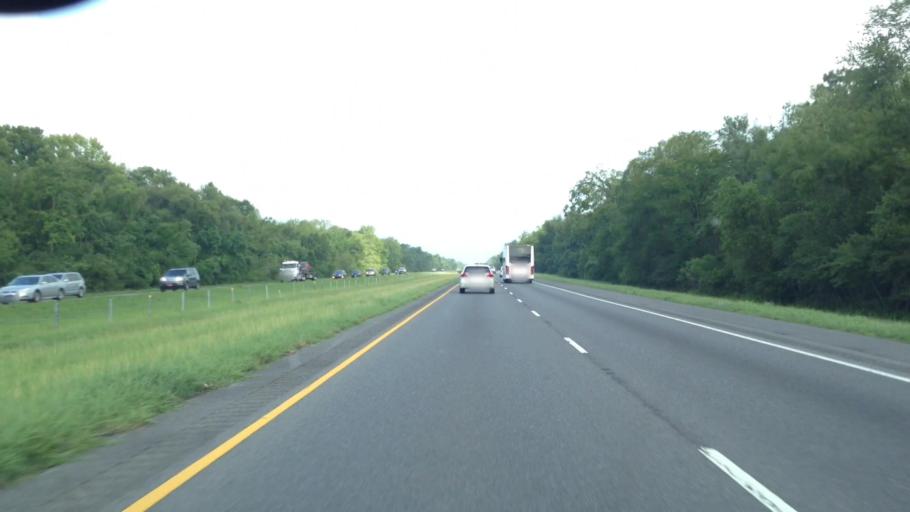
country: US
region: Louisiana
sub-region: Saint James Parish
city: Grand Point
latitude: 30.1347
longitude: -90.7296
